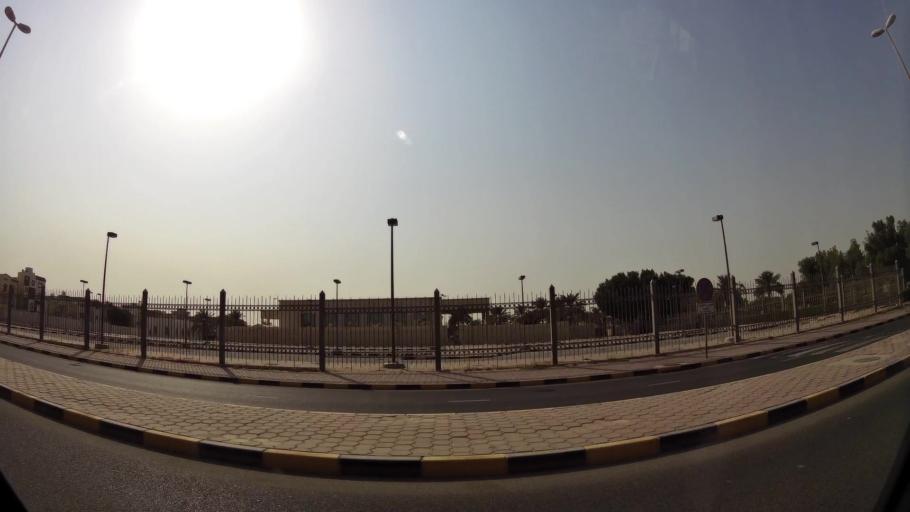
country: KW
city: Bayan
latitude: 29.2891
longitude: 48.0472
